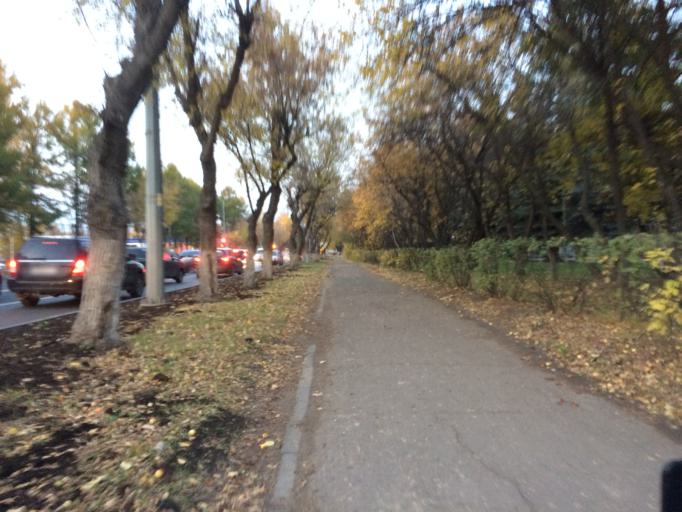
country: RU
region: Mariy-El
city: Yoshkar-Ola
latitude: 56.6127
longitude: 47.8813
